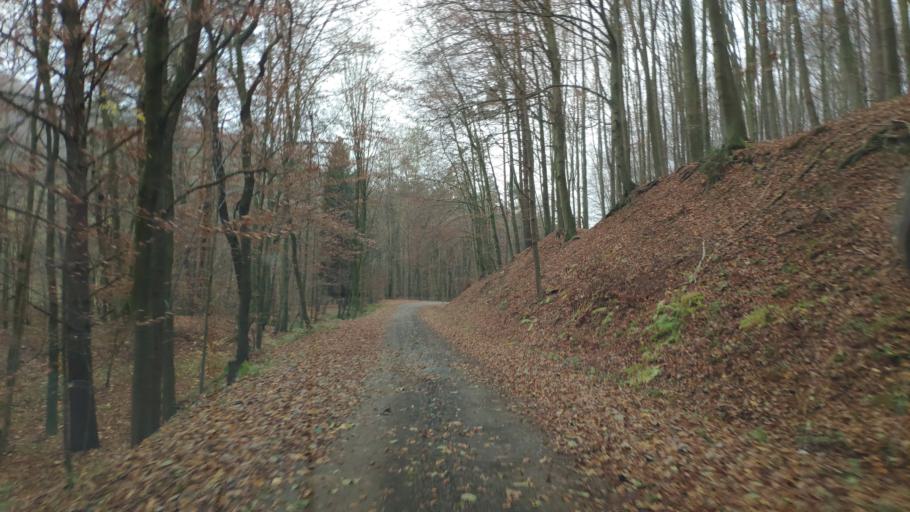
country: SK
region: Presovsky
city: Sabinov
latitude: 49.1475
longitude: 21.2121
